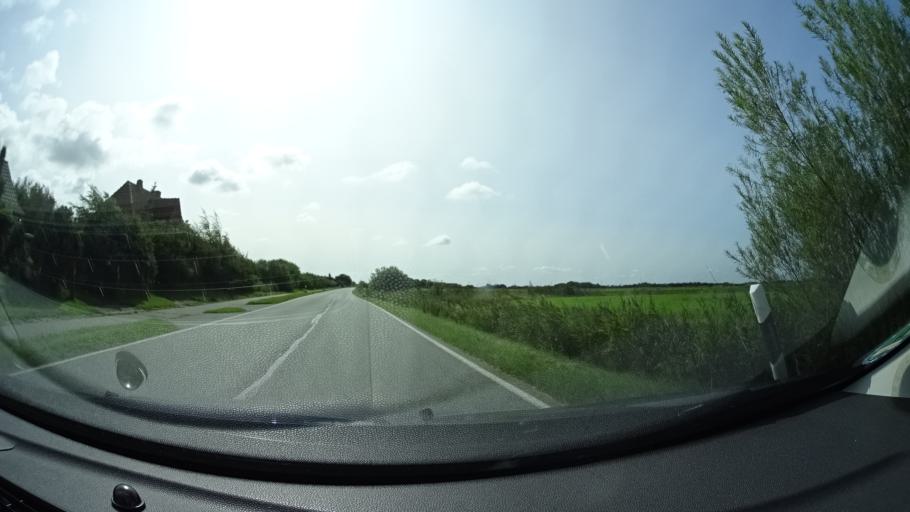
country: DE
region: Schleswig-Holstein
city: Neukirchen
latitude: 54.8827
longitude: 8.7523
